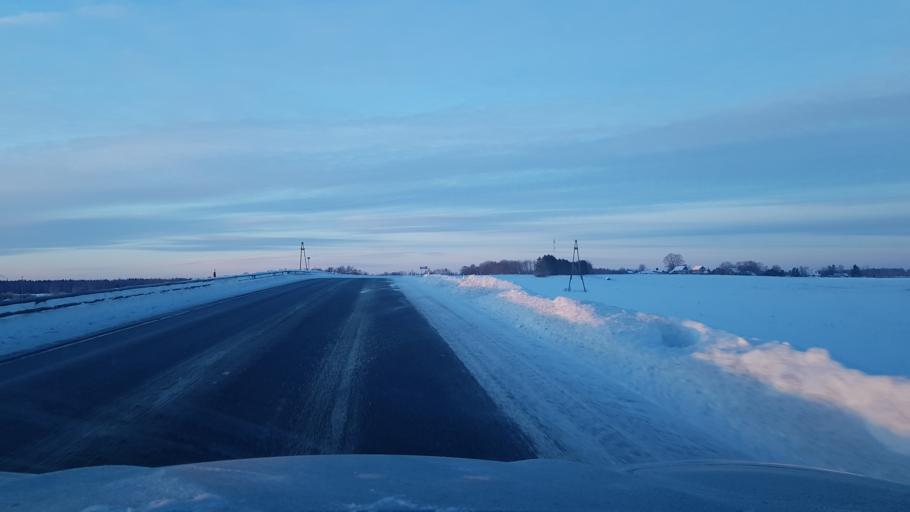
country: EE
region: Ida-Virumaa
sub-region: Narva-Joesuu linn
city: Narva-Joesuu
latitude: 59.3927
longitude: 27.9919
